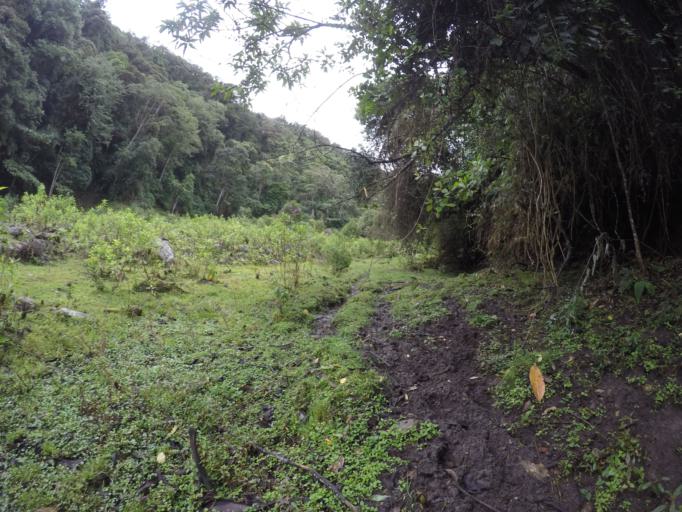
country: CO
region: Tolima
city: Cajamarca
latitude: 4.5254
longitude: -75.3613
